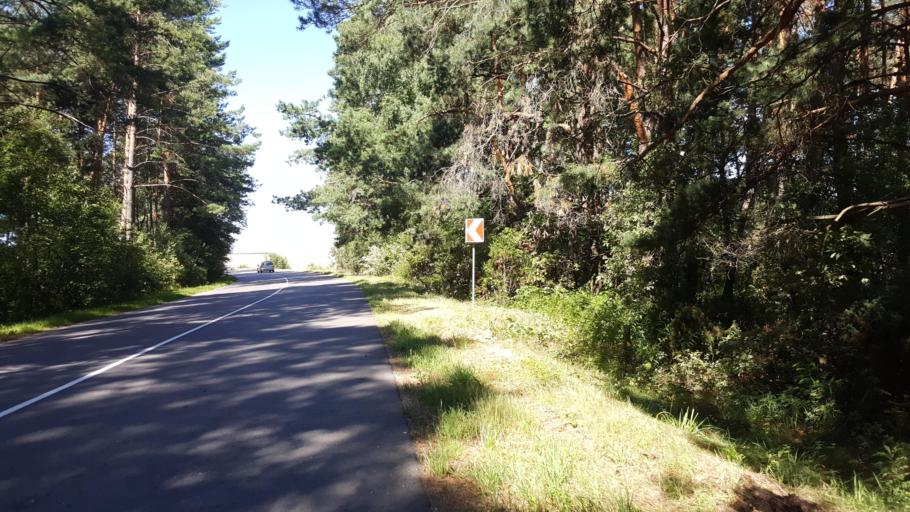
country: BY
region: Brest
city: Kamyanyets
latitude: 52.3802
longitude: 23.6836
